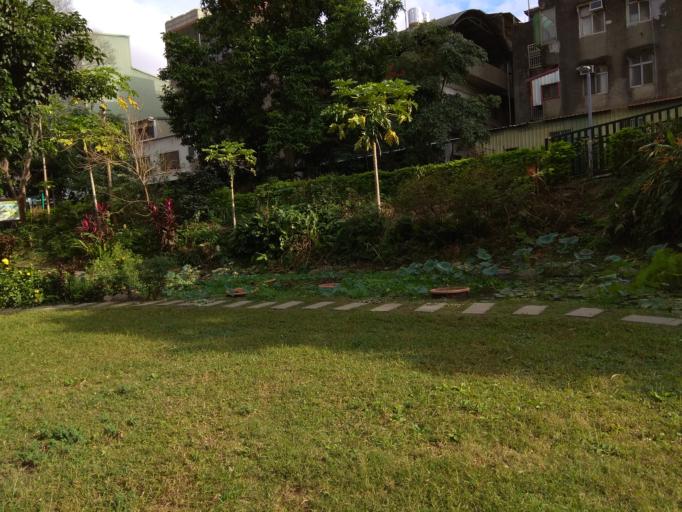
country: TW
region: Taiwan
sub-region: Hsinchu
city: Hsinchu
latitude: 24.7955
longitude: 120.9792
